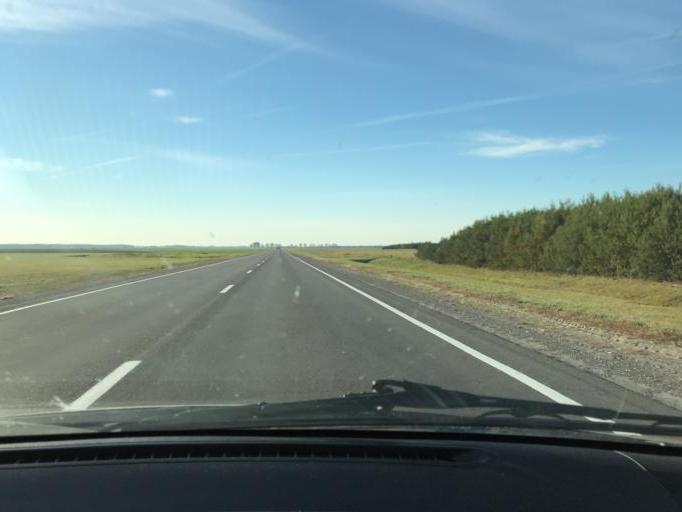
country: BY
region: Brest
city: Antopal'
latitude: 52.2223
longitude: 24.8355
